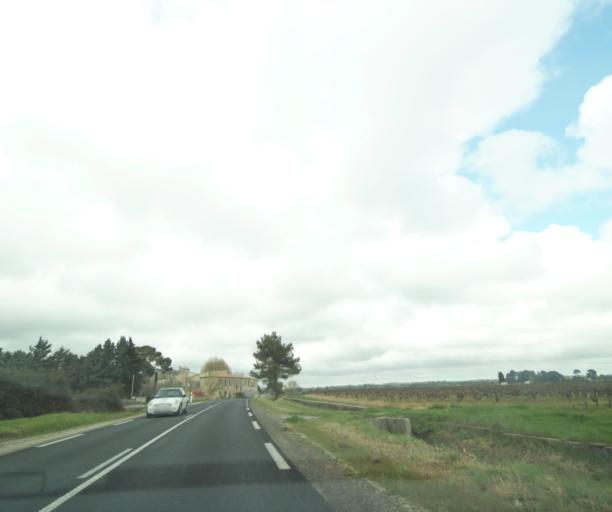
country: FR
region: Languedoc-Roussillon
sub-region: Departement de l'Herault
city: Pignan
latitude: 43.5933
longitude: 3.7750
